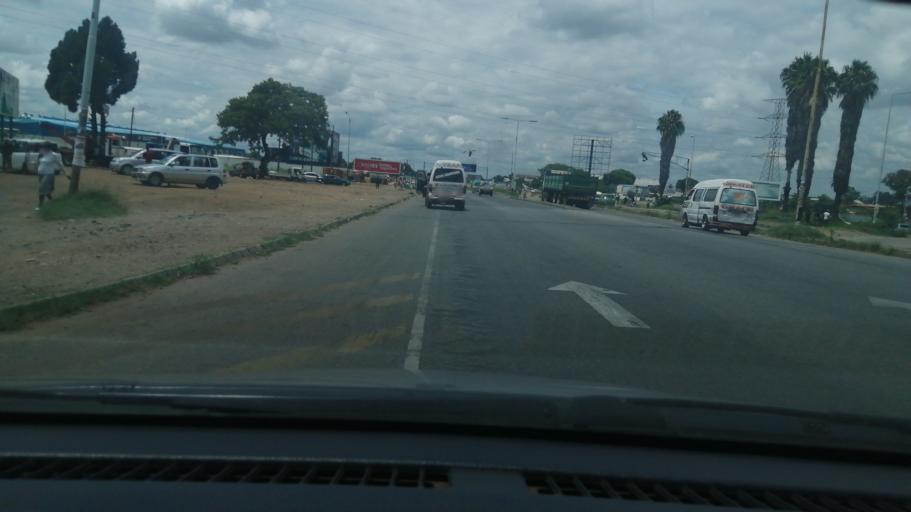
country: ZW
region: Harare
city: Harare
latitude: -17.8729
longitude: 31.0199
